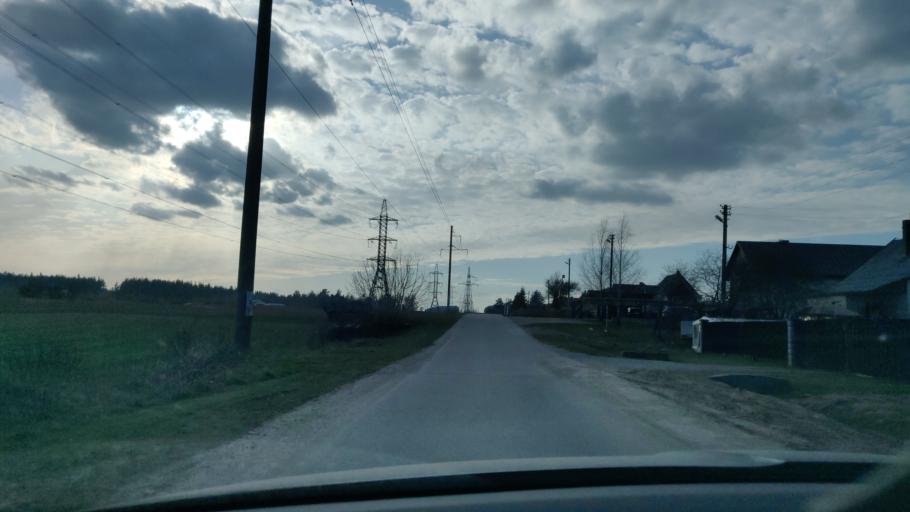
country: LT
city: Trakai
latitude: 54.6052
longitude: 24.9740
